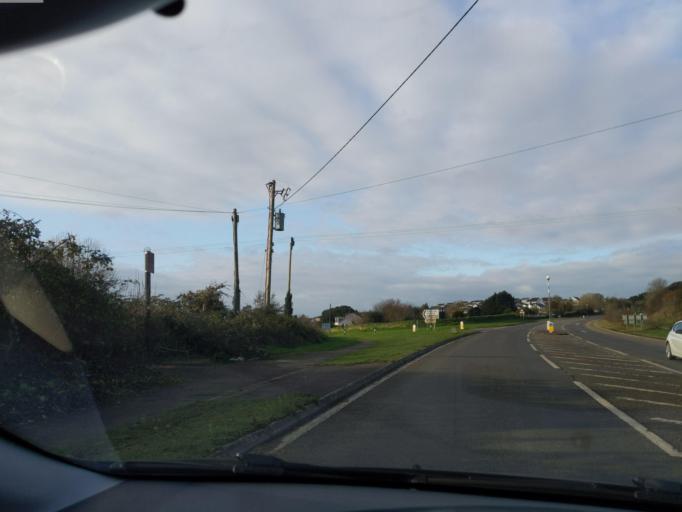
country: GB
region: England
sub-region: Cornwall
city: Wadebridge
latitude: 50.5115
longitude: -4.8160
